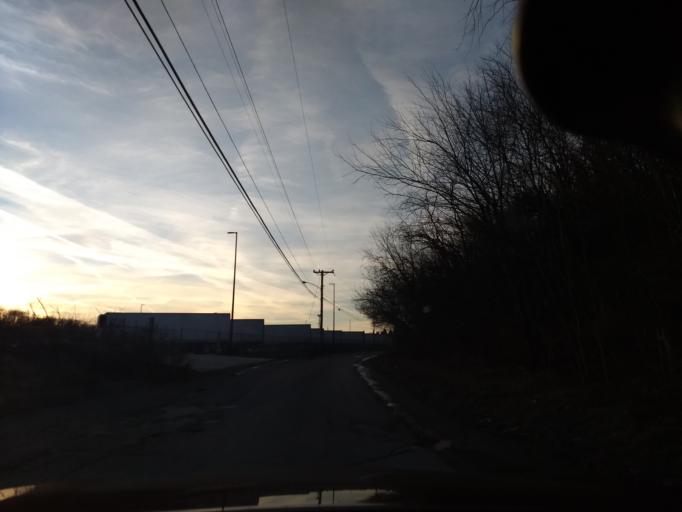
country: US
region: Pennsylvania
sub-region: Allegheny County
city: West Homestead
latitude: 40.3598
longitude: -79.9245
